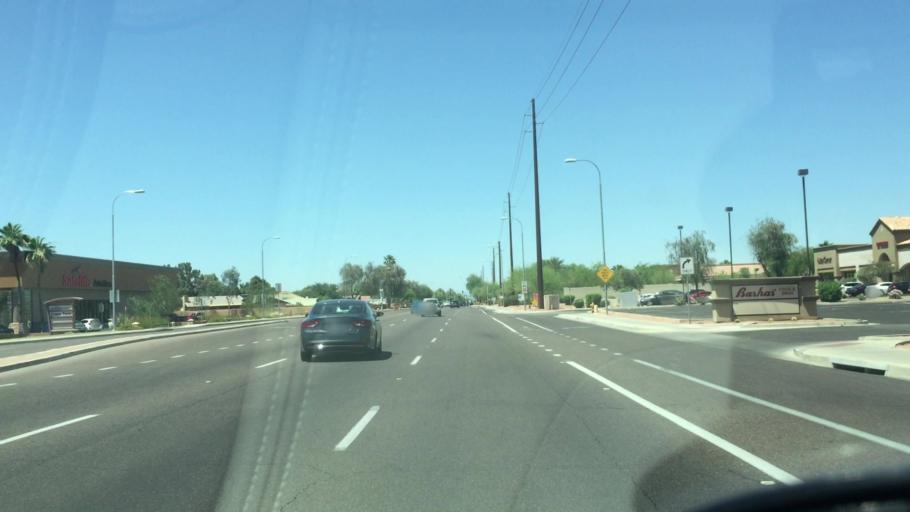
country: US
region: Arizona
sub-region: Maricopa County
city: Chandler
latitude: 33.3066
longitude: -111.8762
